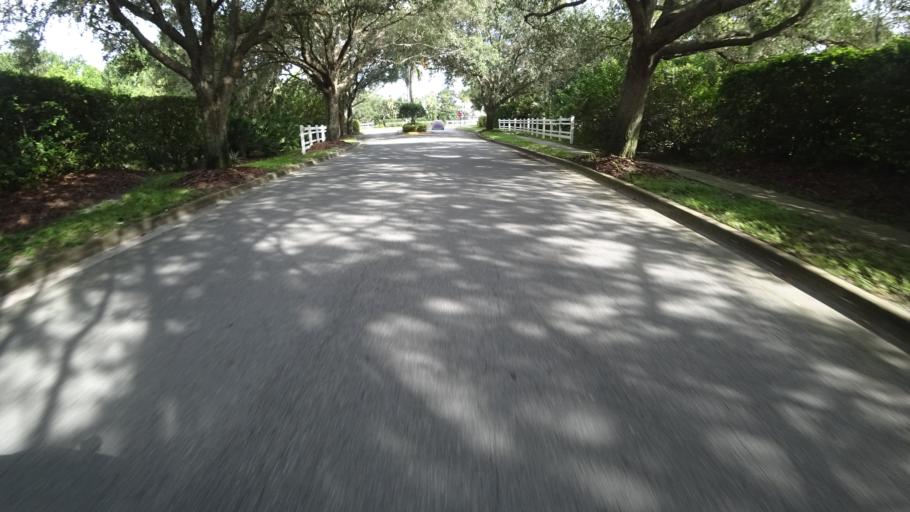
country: US
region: Florida
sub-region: Sarasota County
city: Desoto Lakes
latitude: 27.4156
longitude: -82.4844
